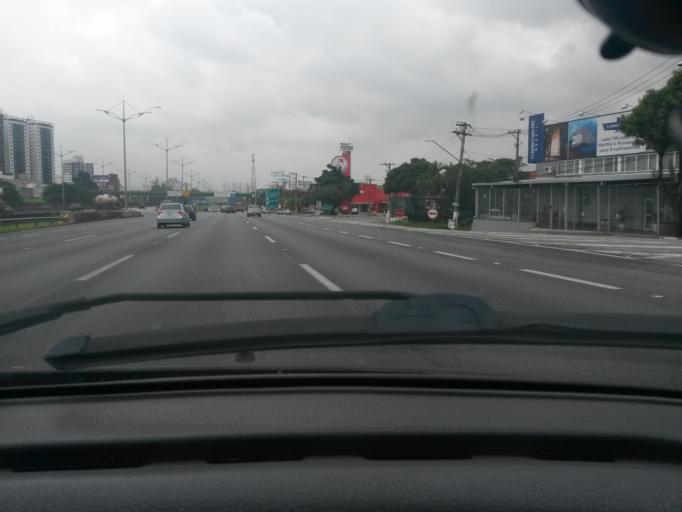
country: BR
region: Sao Paulo
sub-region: Sao Bernardo Do Campo
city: Sao Bernardo do Campo
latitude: -23.6819
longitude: -46.5679
